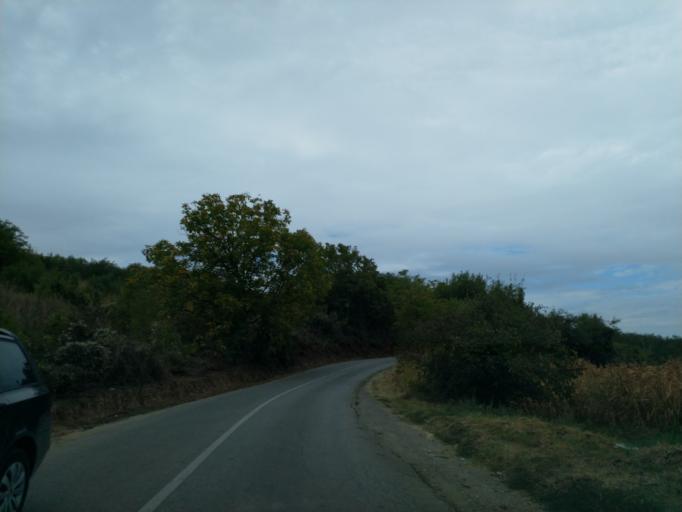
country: RS
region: Central Serbia
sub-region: Pomoravski Okrug
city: Paracin
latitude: 43.8522
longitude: 21.3231
